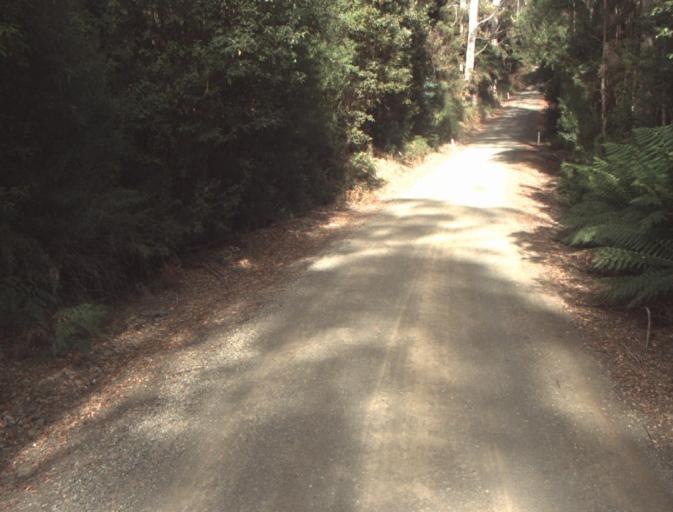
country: AU
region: Tasmania
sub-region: Launceston
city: Mayfield
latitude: -41.2649
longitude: 147.2375
